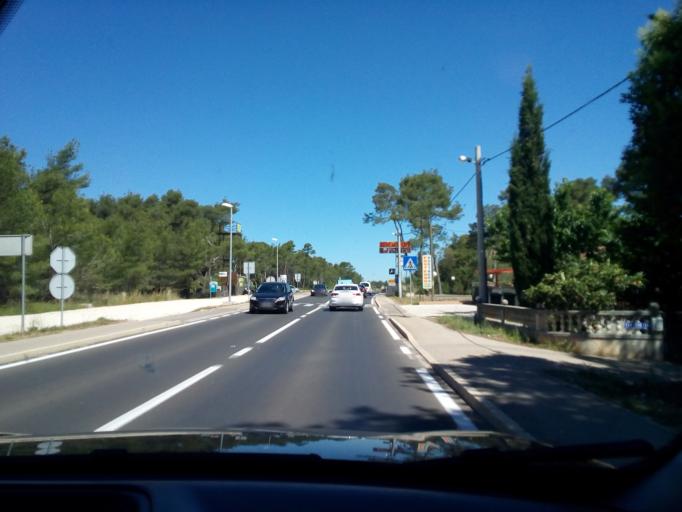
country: HR
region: Zadarska
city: Nin
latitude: 44.1746
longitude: 15.1914
